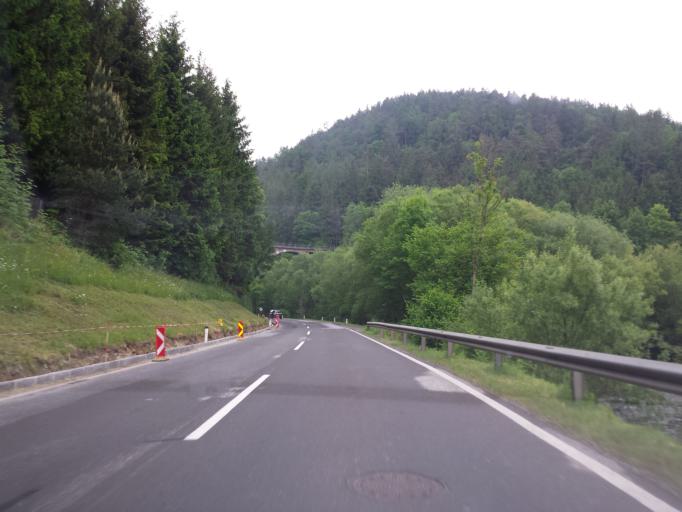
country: AT
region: Styria
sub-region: Politischer Bezirk Weiz
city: Baierdorf-Umgebung
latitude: 47.2576
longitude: 15.7175
